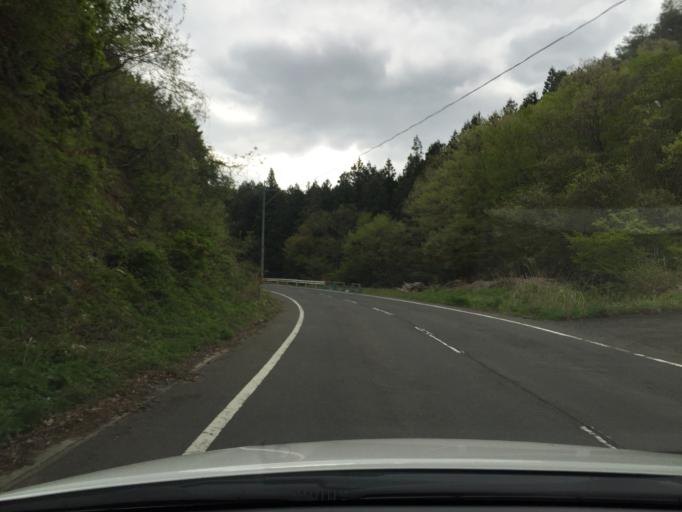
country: JP
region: Fukushima
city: Yanagawamachi-saiwaicho
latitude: 37.7508
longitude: 140.6925
